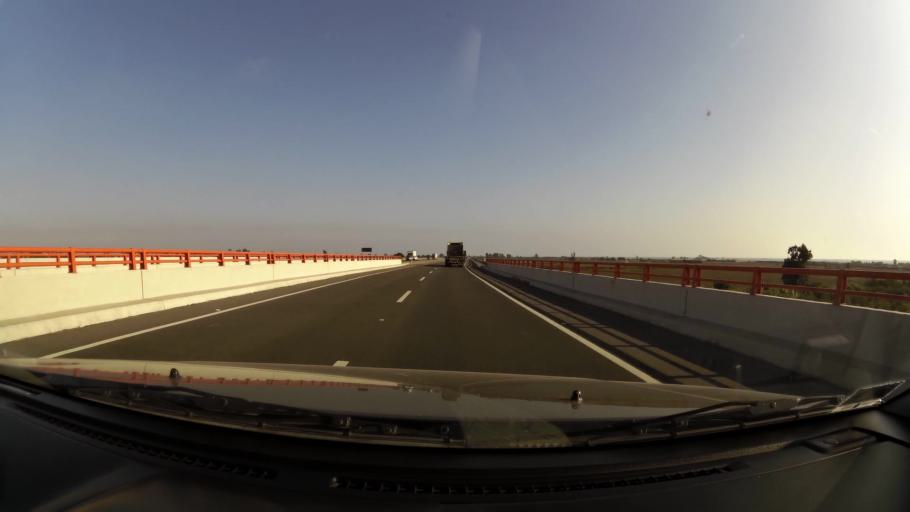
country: PE
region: Ica
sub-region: Provincia de Chincha
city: Chincha Baja
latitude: -13.4630
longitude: -76.1795
